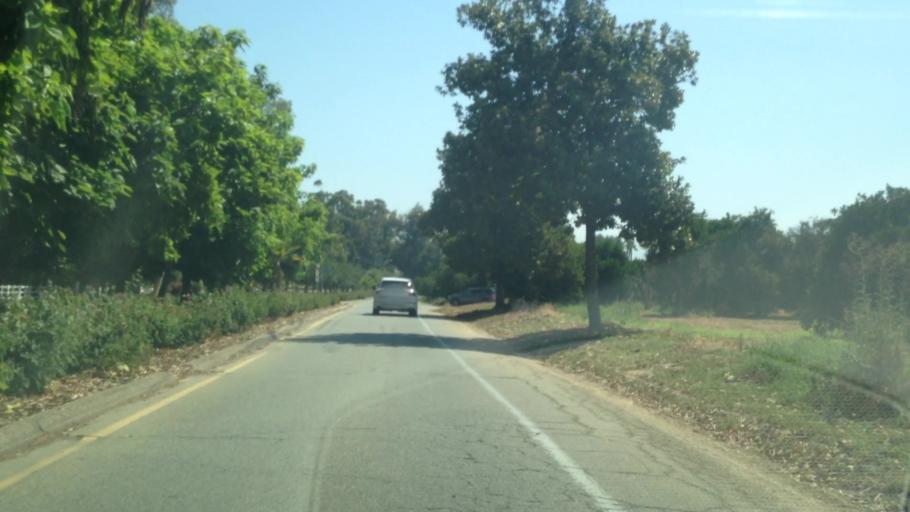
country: US
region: California
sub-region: Riverside County
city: Home Gardens
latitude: 33.8937
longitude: -117.4530
